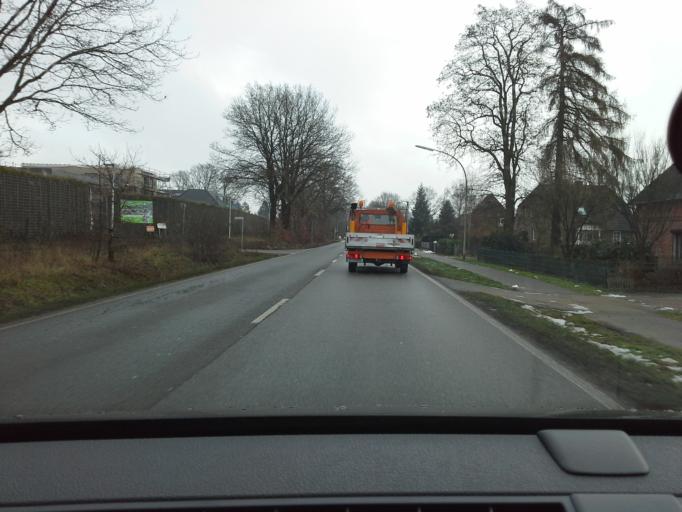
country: DE
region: Schleswig-Holstein
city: Ellerau
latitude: 53.7492
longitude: 9.9353
